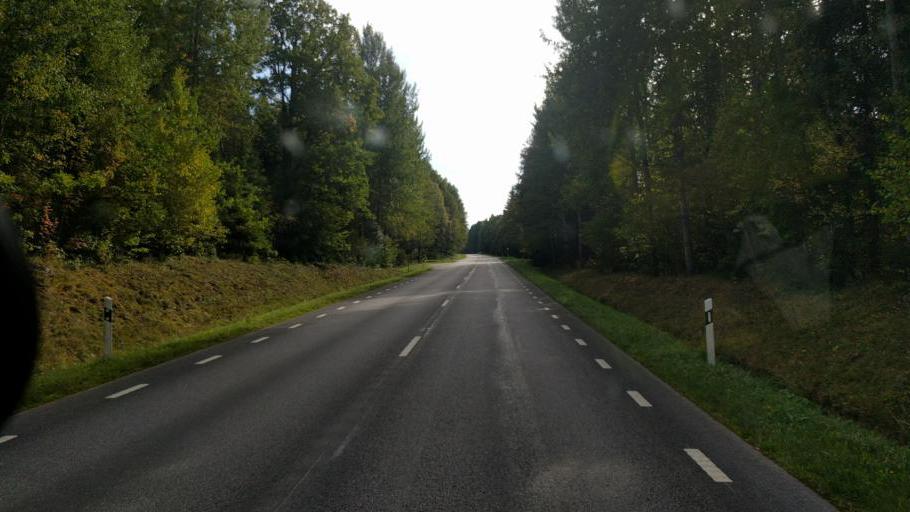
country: SE
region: OEstergoetland
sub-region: Kinda Kommun
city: Kisa
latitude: 57.9426
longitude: 15.6670
